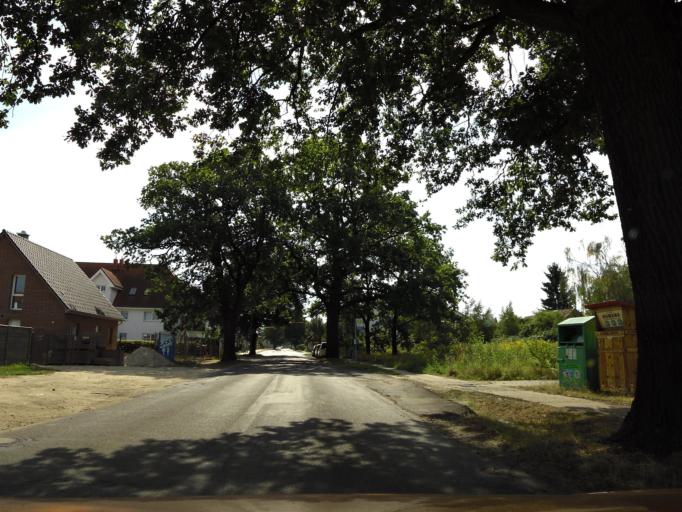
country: DE
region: Brandenburg
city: Teltow
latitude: 52.3783
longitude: 13.2614
